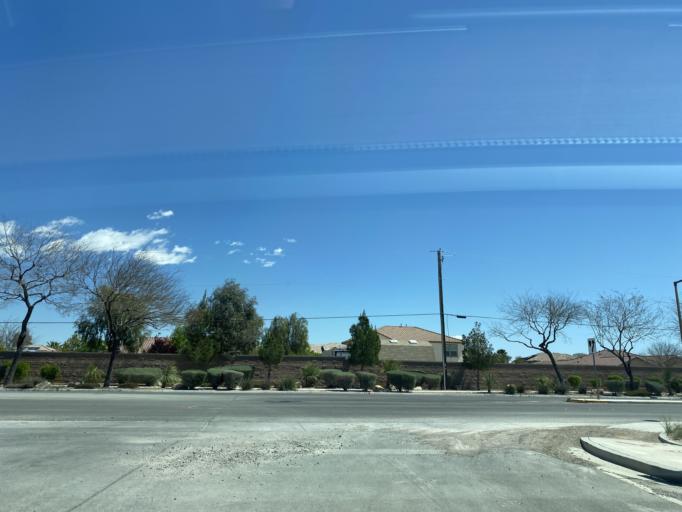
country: US
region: Nevada
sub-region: Clark County
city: North Las Vegas
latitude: 36.3107
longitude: -115.2246
